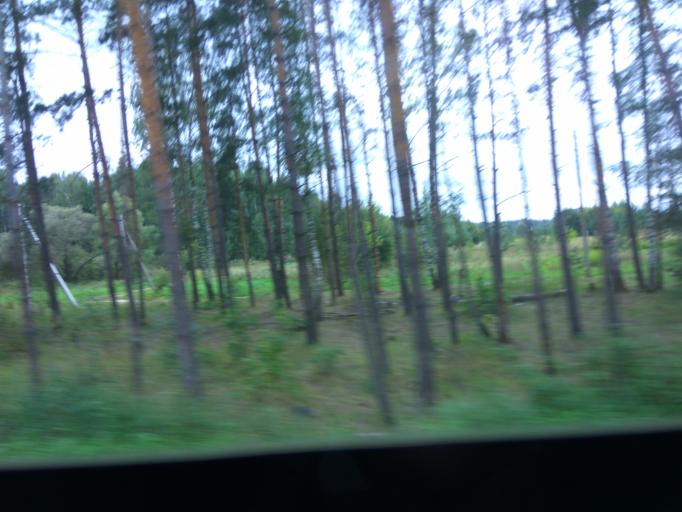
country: RU
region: Moskovskaya
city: Malyshevo
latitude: 55.5258
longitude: 38.3422
